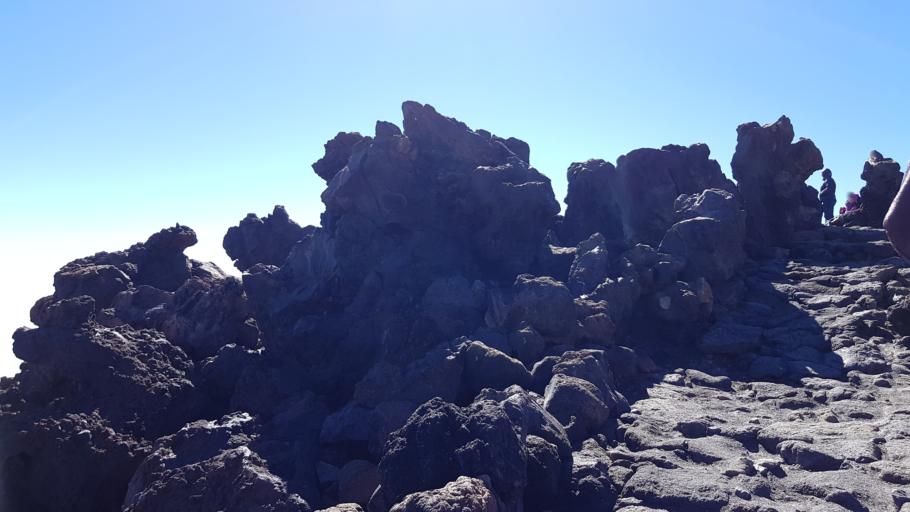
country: ES
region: Canary Islands
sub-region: Provincia de Santa Cruz de Tenerife
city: La Guancha
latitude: 28.2719
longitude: -16.6384
